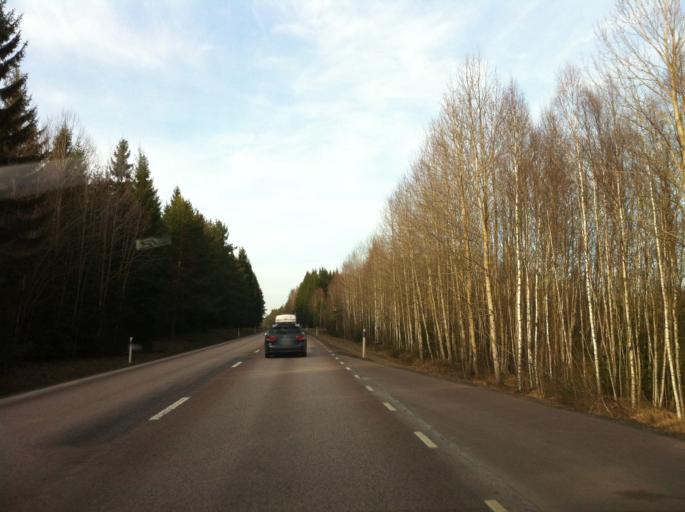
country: SE
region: Vaermland
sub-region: Kristinehamns Kommun
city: Bjorneborg
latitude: 59.2200
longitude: 14.1840
